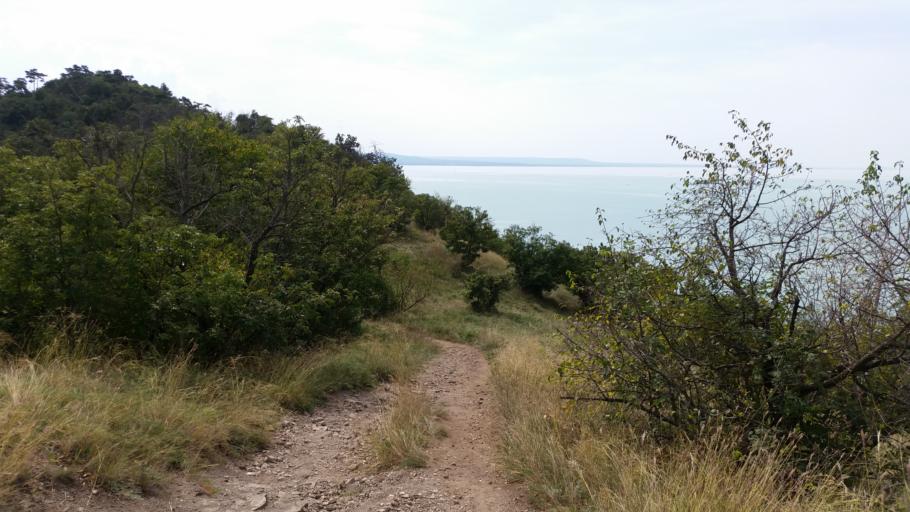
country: HU
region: Veszprem
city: Tihany
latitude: 46.9092
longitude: 17.8522
